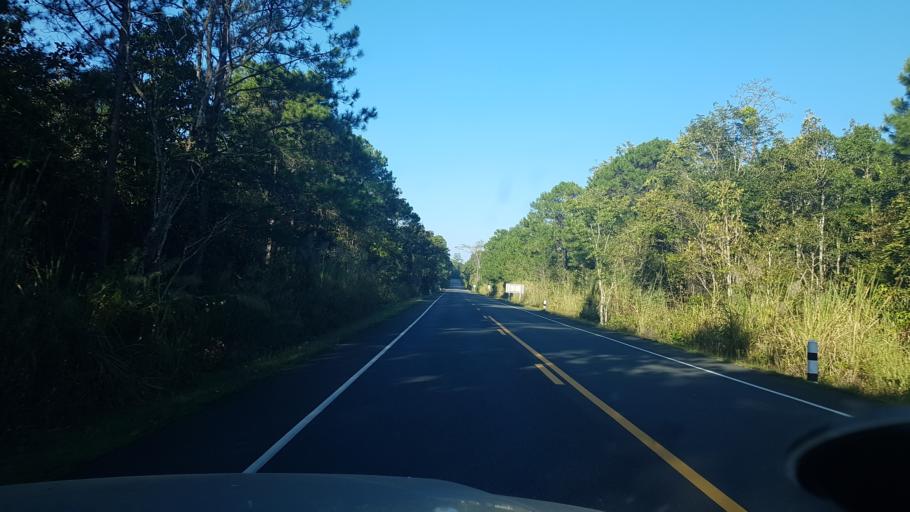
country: TH
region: Phetchabun
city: Nam Nao
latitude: 16.7260
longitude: 101.5805
